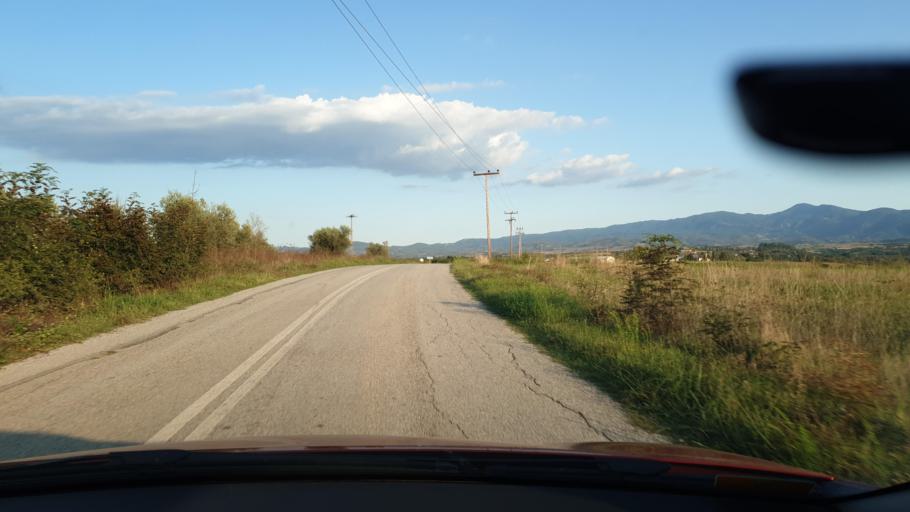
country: GR
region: Central Macedonia
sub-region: Nomos Thessalonikis
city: Nea Apollonia
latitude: 40.5552
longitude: 23.4386
